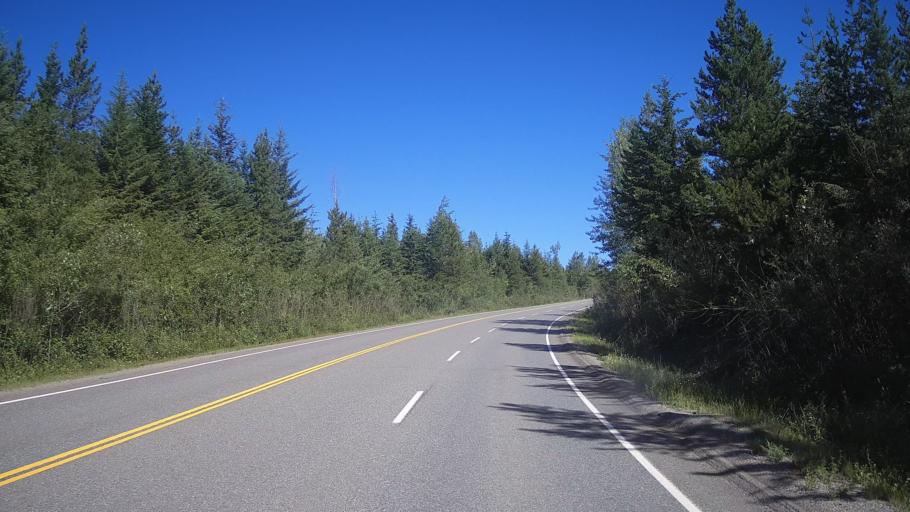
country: CA
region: British Columbia
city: Kamloops
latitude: 51.4886
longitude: -120.3230
